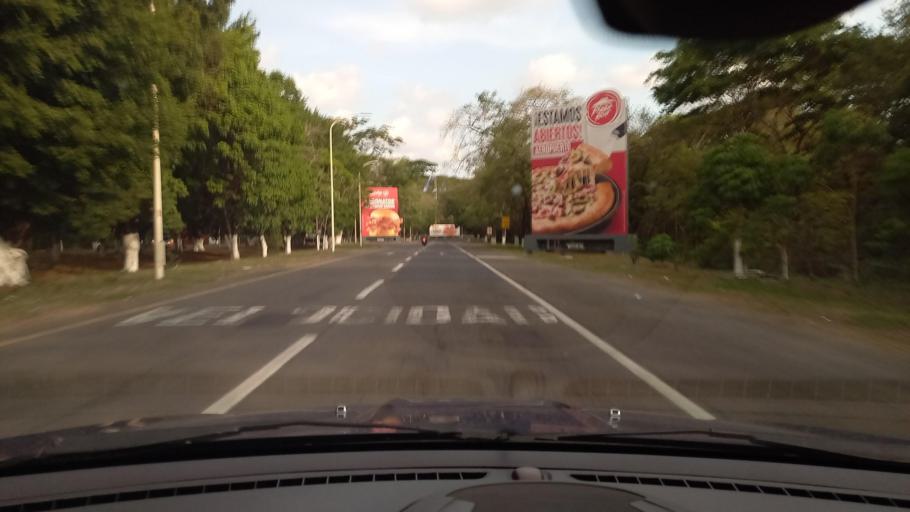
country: SV
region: La Paz
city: El Rosario
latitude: 13.4521
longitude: -89.0600
